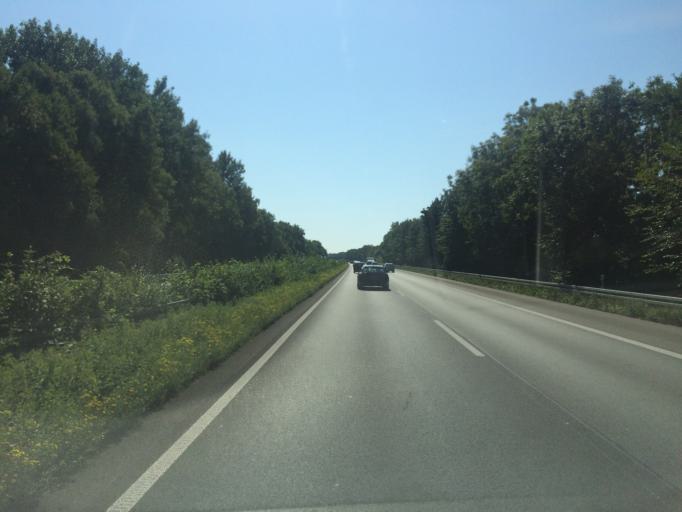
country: DE
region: North Rhine-Westphalia
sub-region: Regierungsbezirk Munster
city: Ascheberg
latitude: 51.7678
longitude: 7.6408
